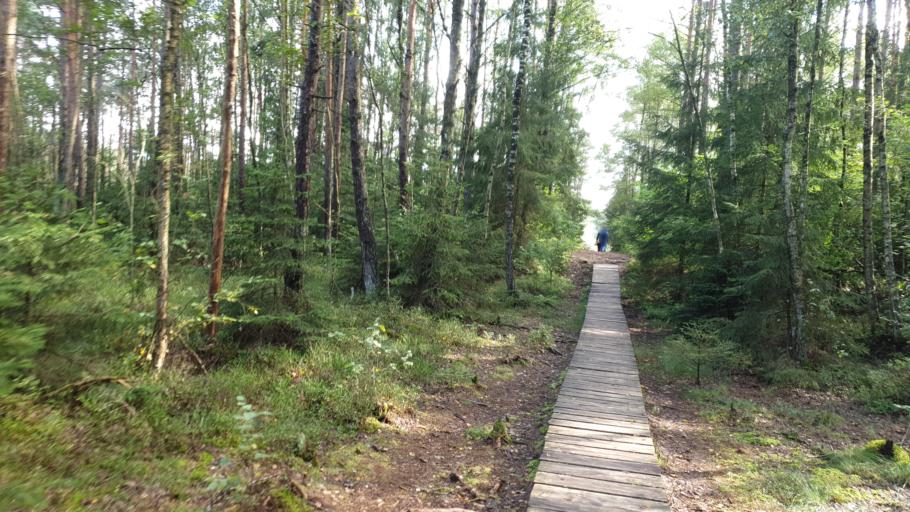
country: LT
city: Trakai
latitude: 54.6435
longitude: 24.9676
